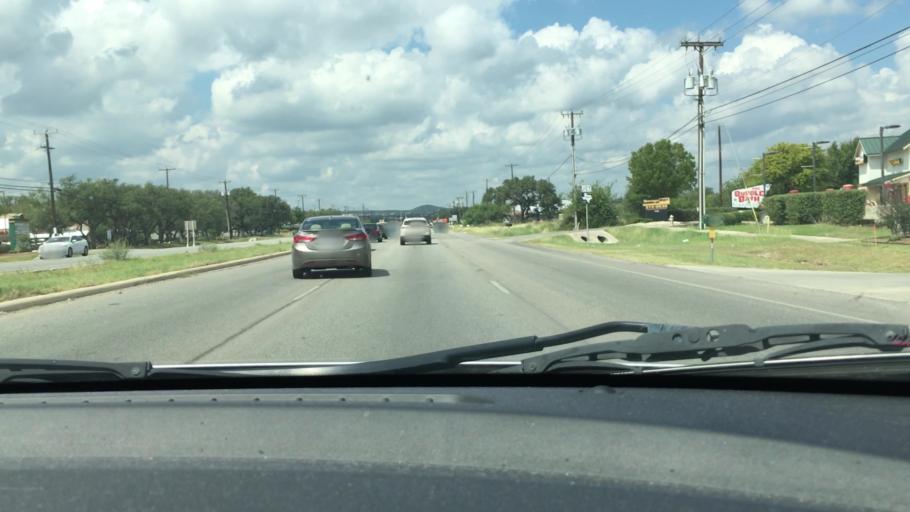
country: US
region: Texas
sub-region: Bexar County
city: Helotes
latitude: 29.5591
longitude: -98.6749
